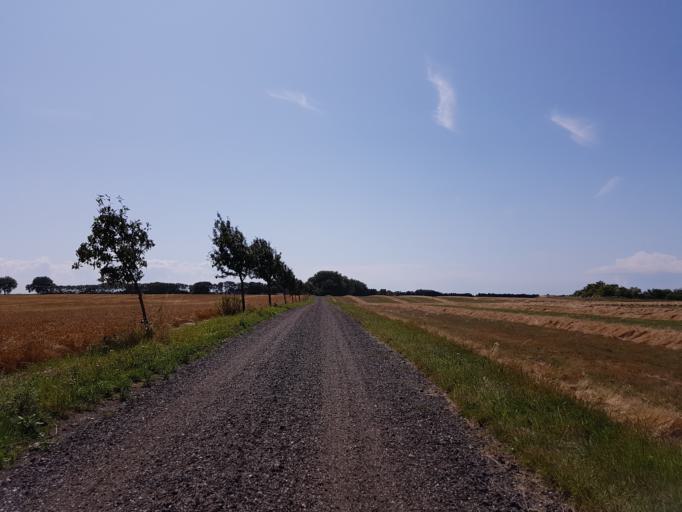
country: DK
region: Zealand
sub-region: Guldborgsund Kommune
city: Nykobing Falster
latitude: 54.5726
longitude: 11.9539
